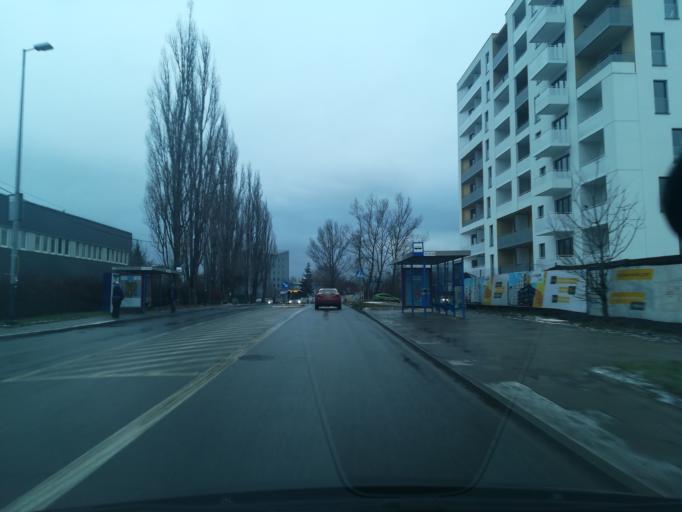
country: PL
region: Lesser Poland Voivodeship
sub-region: Krakow
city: Krakow
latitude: 50.0238
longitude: 19.9604
